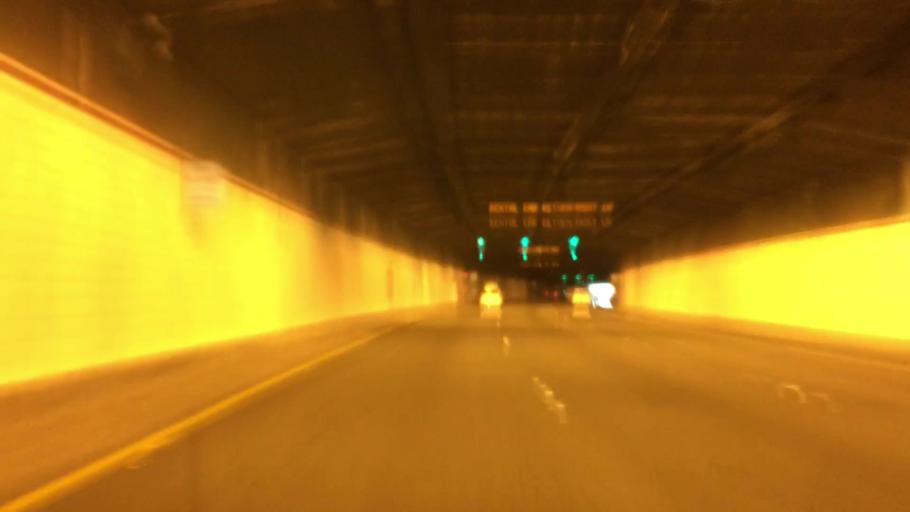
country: US
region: Nevada
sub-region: Clark County
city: Paradise
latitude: 36.0785
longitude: -115.1435
